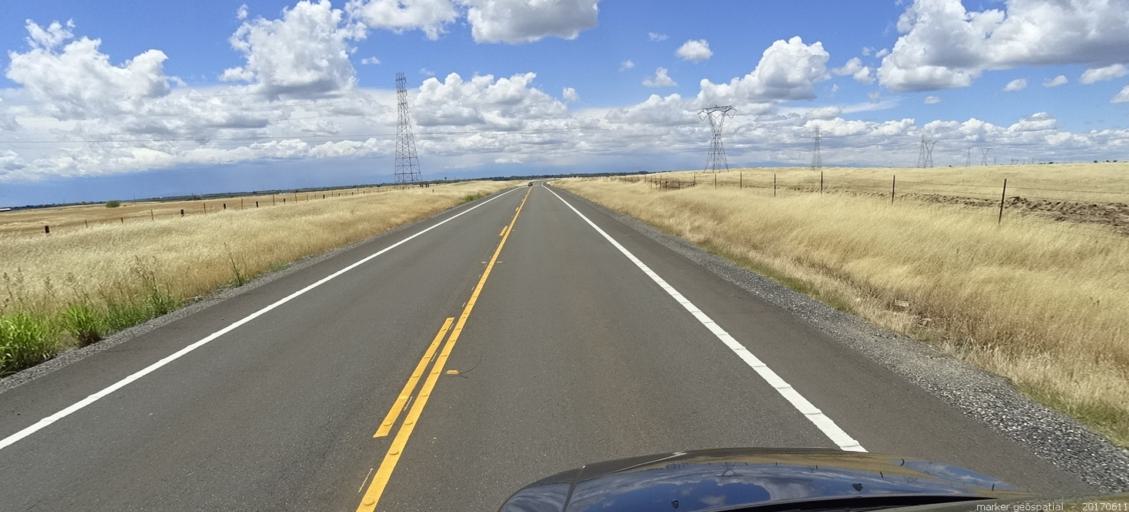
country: US
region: California
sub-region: Butte County
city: Durham
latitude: 39.6393
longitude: -121.6989
